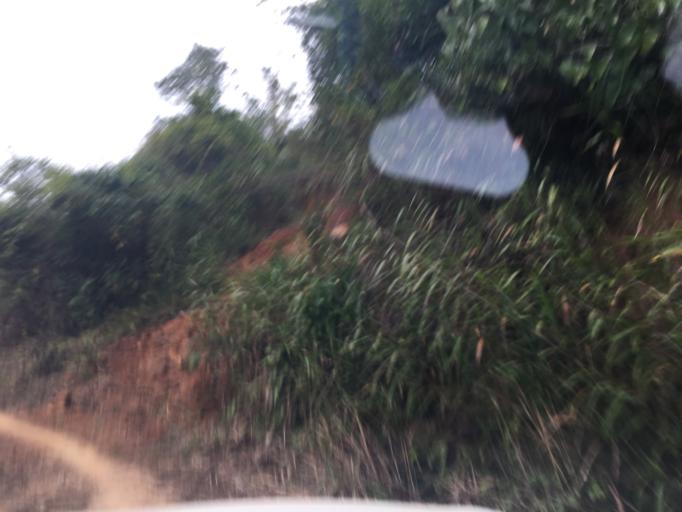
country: LA
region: Houaphan
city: Viengthong
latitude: 19.9375
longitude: 103.2981
